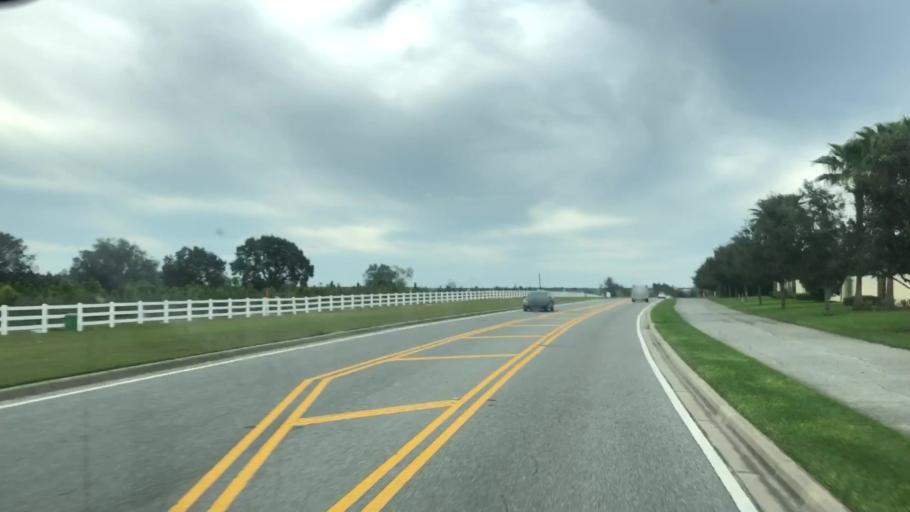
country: US
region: Florida
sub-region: Orange County
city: Lake Butler
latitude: 28.4535
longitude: -81.6238
